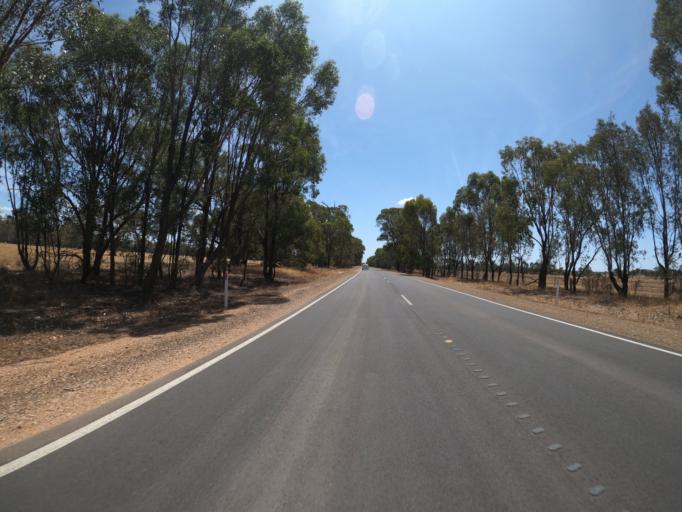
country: AU
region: Victoria
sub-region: Benalla
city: Benalla
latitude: -36.4937
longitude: 146.0178
